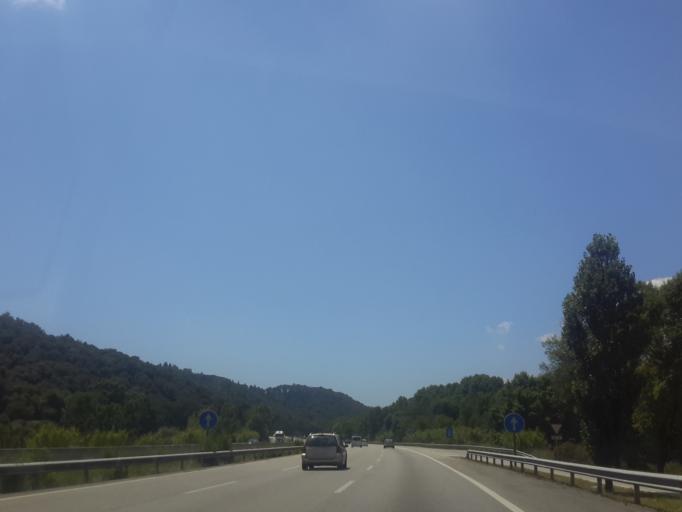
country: ES
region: Catalonia
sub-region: Provincia de Barcelona
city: Sant Celoni
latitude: 41.7007
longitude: 2.5172
